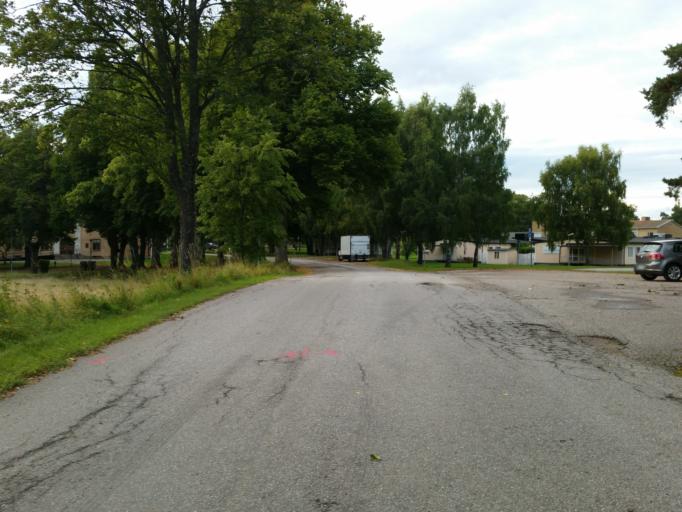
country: SE
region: Stockholm
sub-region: Upplands Vasby Kommun
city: Upplands Vaesby
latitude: 59.5394
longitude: 17.9162
